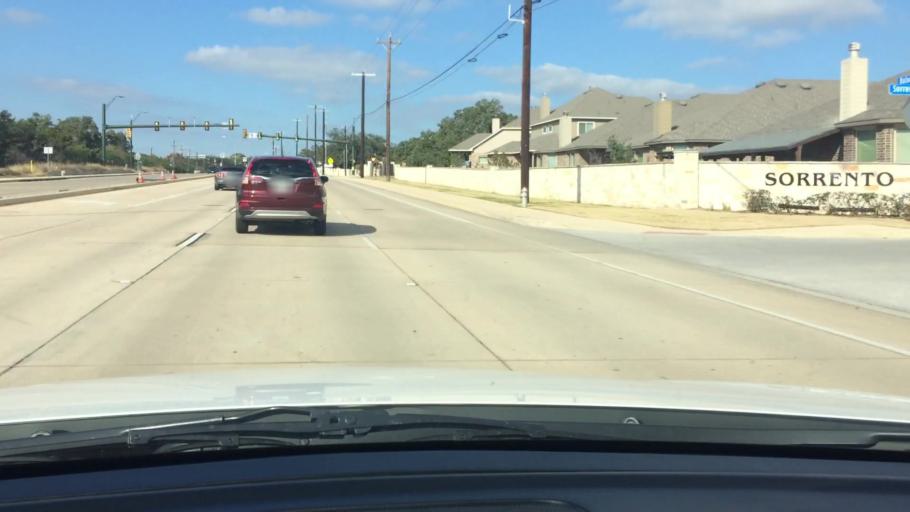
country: US
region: Texas
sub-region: Bexar County
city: Hollywood Park
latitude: 29.6370
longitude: -98.4239
